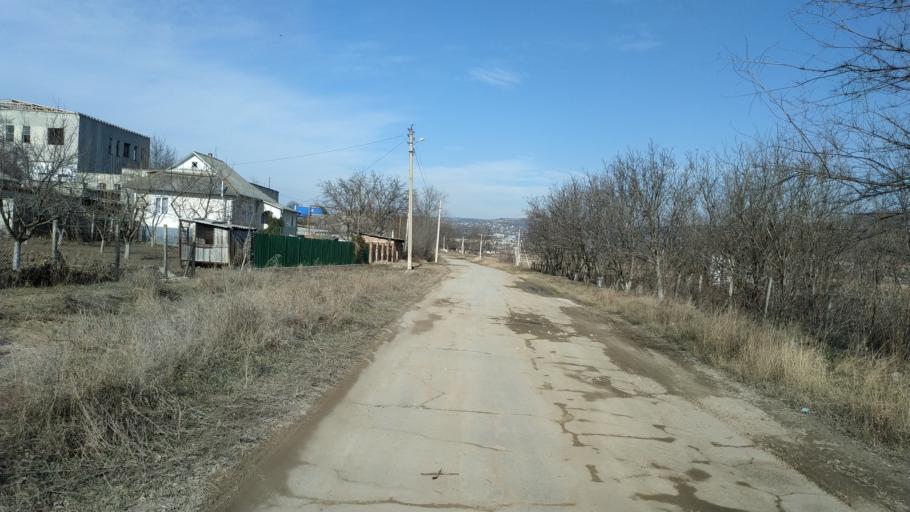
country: MD
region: Nisporeni
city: Nisporeni
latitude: 47.0610
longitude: 28.1710
